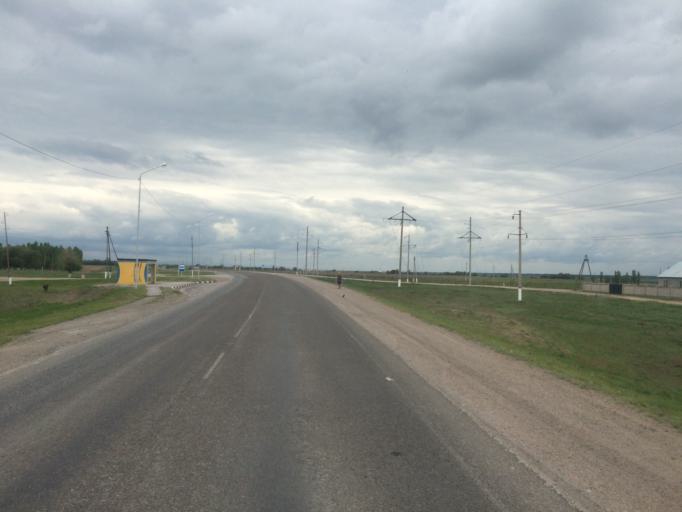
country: KG
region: Chuy
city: Sokuluk
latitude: 43.2469
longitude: 74.2986
